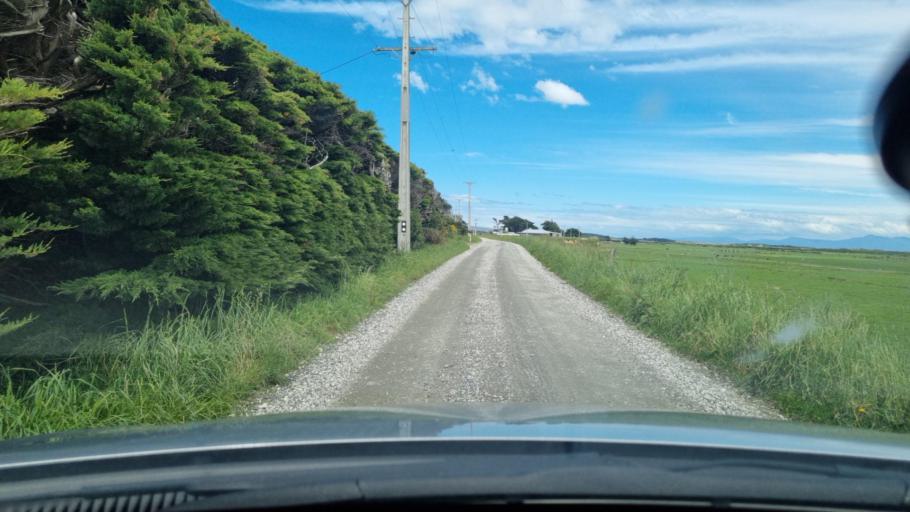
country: NZ
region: Southland
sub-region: Invercargill City
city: Invercargill
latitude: -46.3949
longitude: 168.2578
